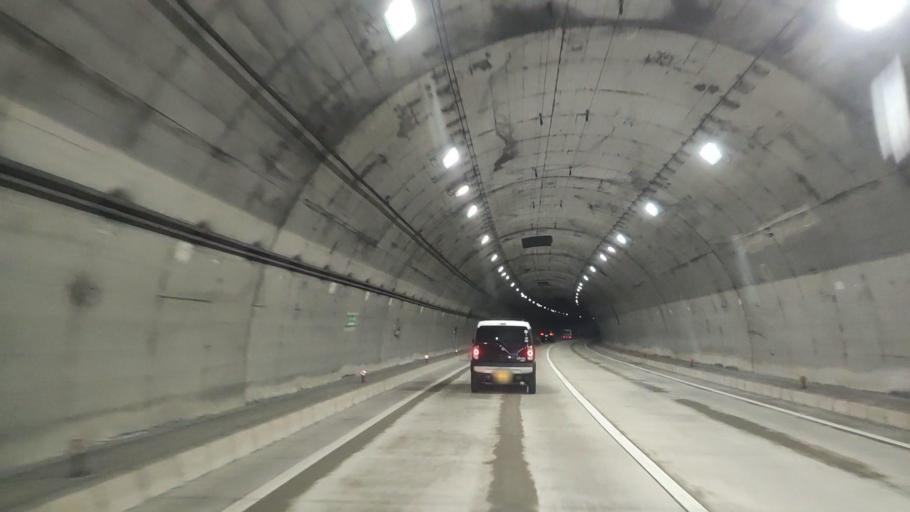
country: JP
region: Hiroshima
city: Onomichi
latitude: 34.4455
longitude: 133.2280
